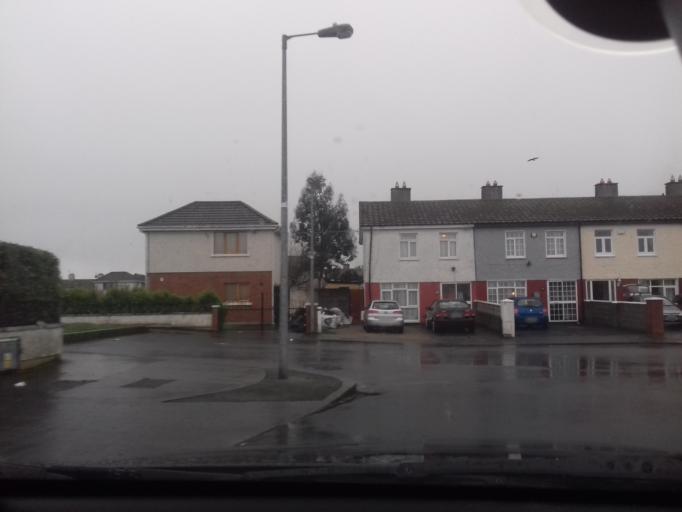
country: IE
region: Leinster
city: Hartstown
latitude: 53.3928
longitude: -6.4048
